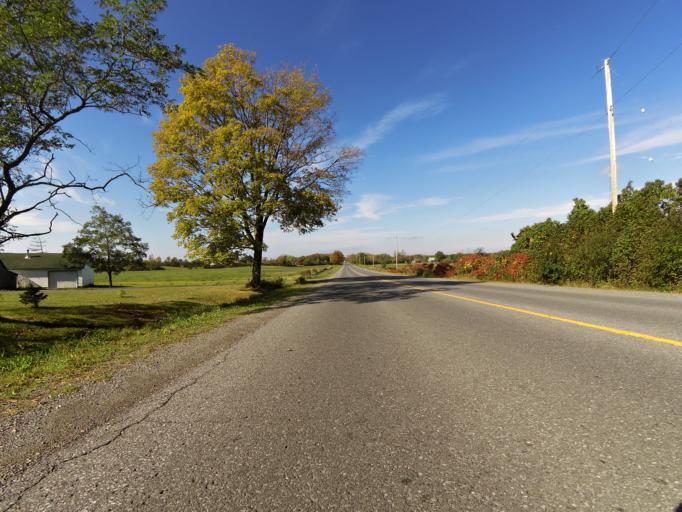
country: CA
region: Ontario
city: Prince Edward
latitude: 44.0147
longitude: -77.3098
